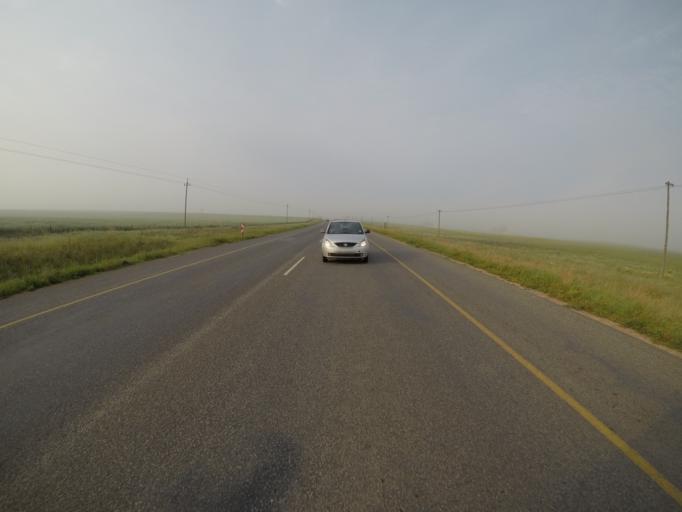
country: ZA
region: Western Cape
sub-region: City of Cape Town
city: Kraaifontein
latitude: -33.6566
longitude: 18.7084
